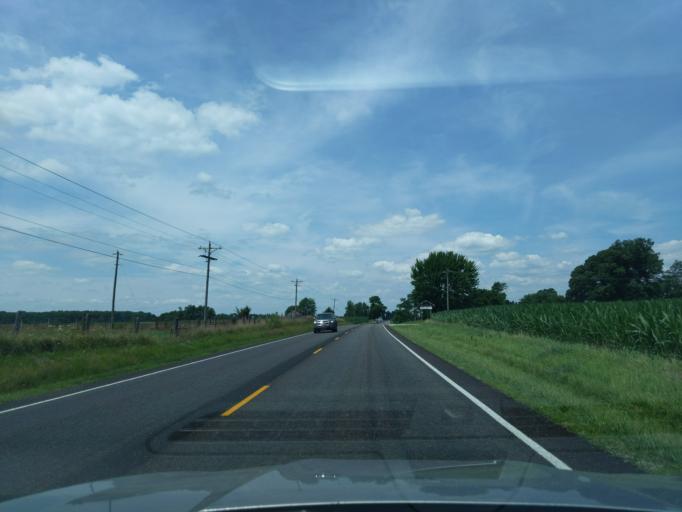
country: US
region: Indiana
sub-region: Ripley County
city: Osgood
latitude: 39.2113
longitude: -85.3319
